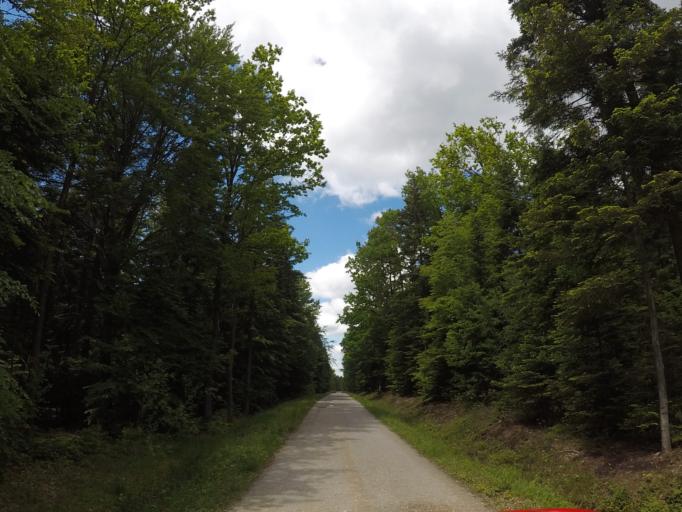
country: PL
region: Swietokrzyskie
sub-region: Powiat kielecki
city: Kielce
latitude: 50.9143
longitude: 20.6500
